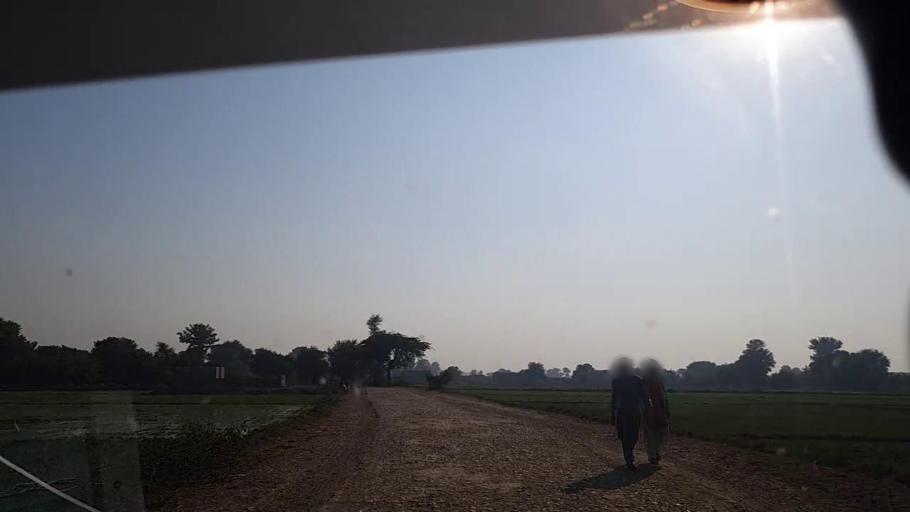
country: PK
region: Sindh
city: Hingorja
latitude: 27.2151
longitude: 68.2644
